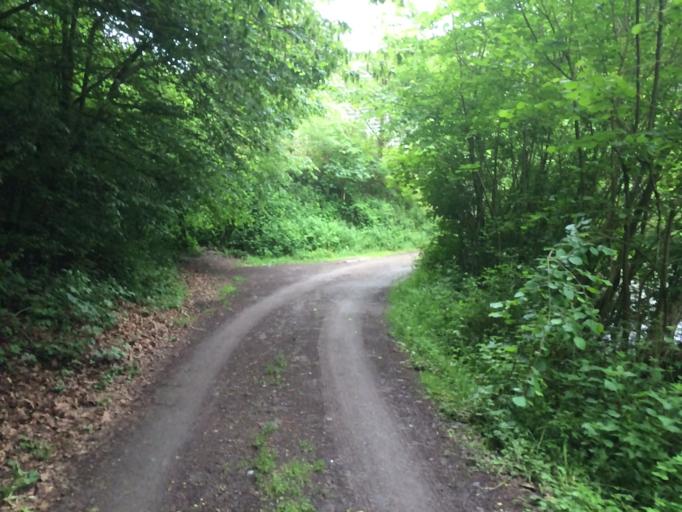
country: BE
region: Wallonia
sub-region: Province de Namur
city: Yvoir
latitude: 50.3235
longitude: 4.9425
